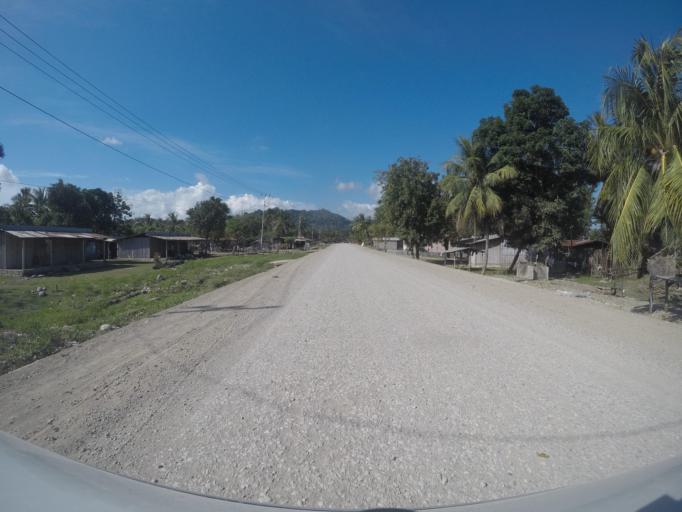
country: TL
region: Viqueque
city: Viqueque
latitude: -8.8122
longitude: 126.5380
